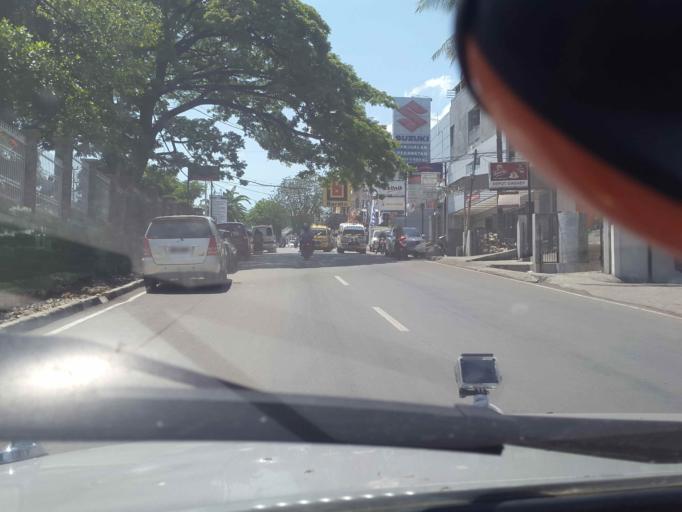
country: ID
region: East Nusa Tenggara
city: Fontein
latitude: -10.1682
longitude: 123.5847
